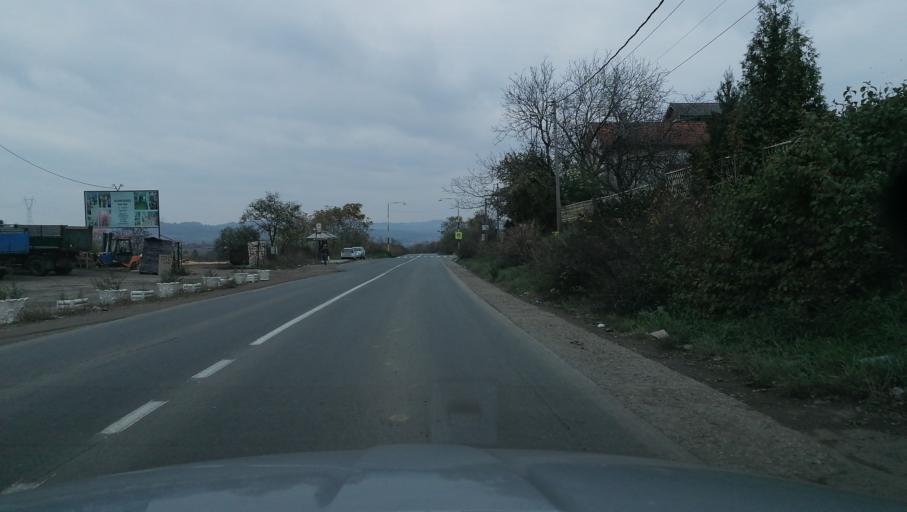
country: RS
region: Central Serbia
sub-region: Belgrade
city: Zvezdara
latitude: 44.7571
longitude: 20.5749
